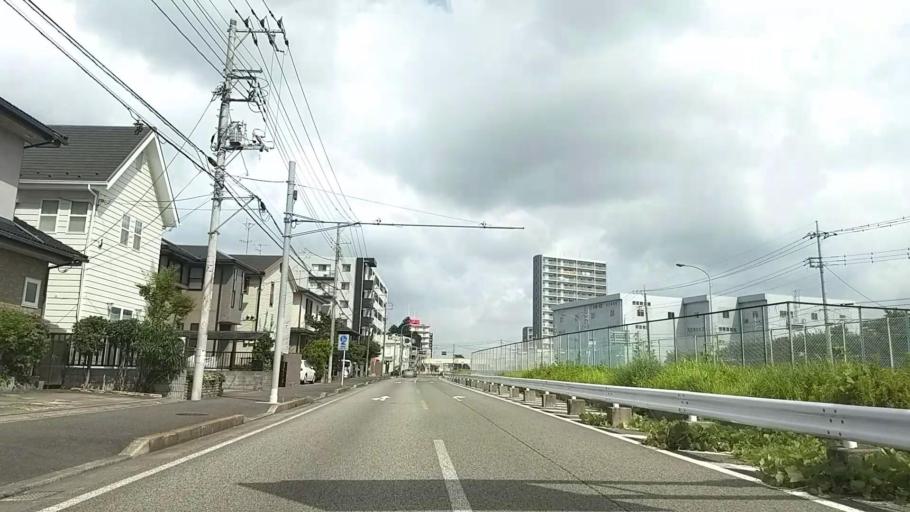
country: JP
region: Tokyo
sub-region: Machida-shi
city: Machida
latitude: 35.5152
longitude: 139.4565
